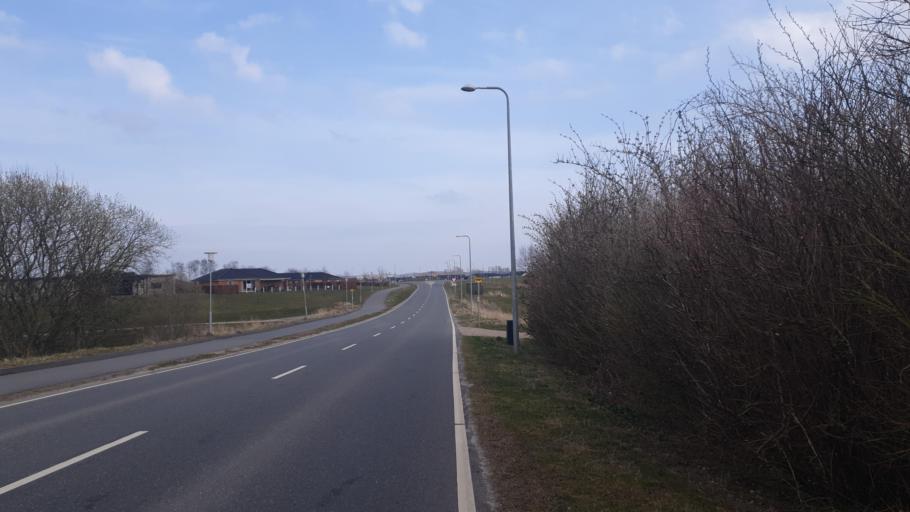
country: DK
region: Central Jutland
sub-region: Hedensted Kommune
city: Hedensted
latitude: 55.7640
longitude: 9.7204
